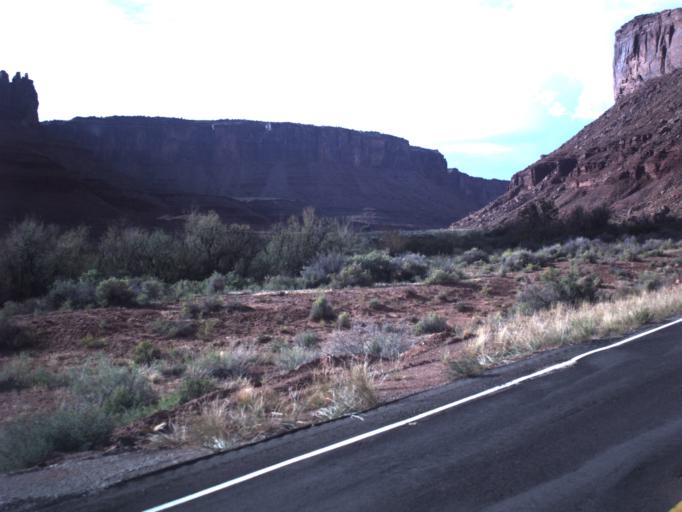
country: US
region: Utah
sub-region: Grand County
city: Moab
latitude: 38.7658
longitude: -109.3202
